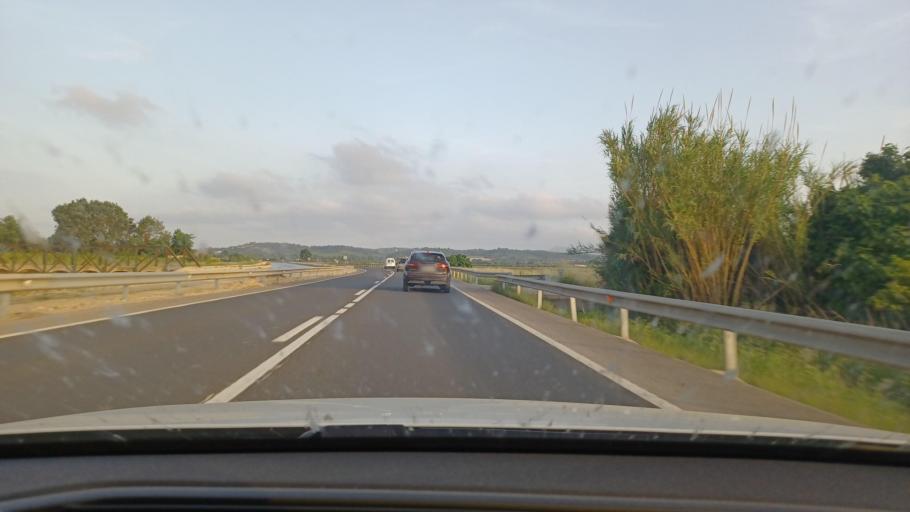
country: ES
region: Catalonia
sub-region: Provincia de Tarragona
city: Masdenverge
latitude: 40.7612
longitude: 0.5352
